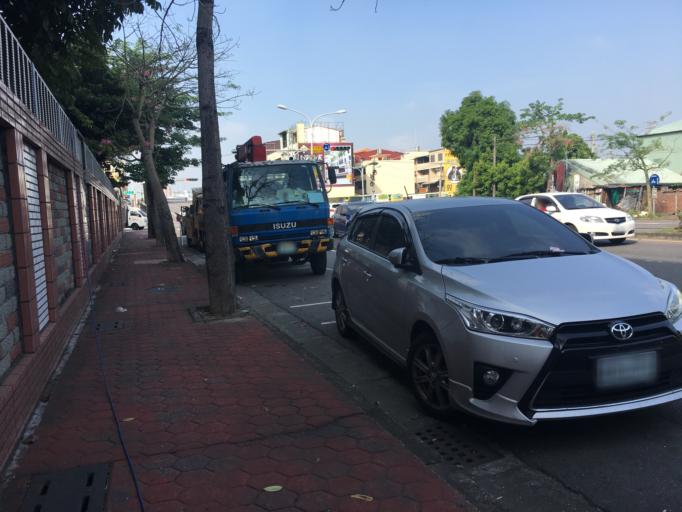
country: TW
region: Taiwan
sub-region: Changhua
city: Chang-hua
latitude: 24.0868
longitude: 120.5516
